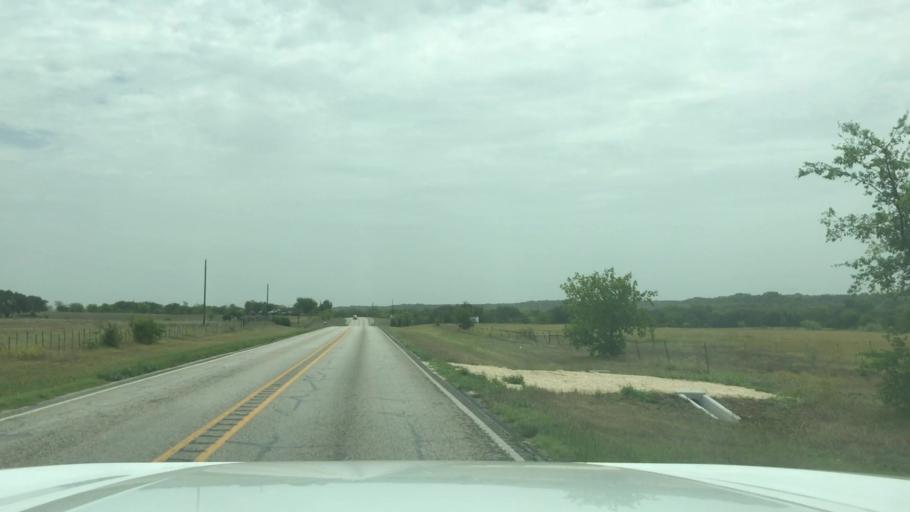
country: US
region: Texas
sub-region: Hamilton County
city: Hico
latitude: 32.0444
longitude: -98.1402
